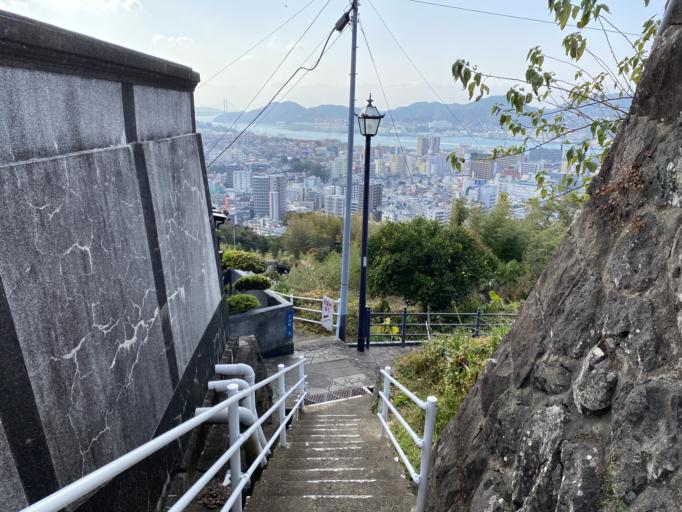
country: JP
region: Nagasaki
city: Nagasaki-shi
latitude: 32.7437
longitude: 129.8858
